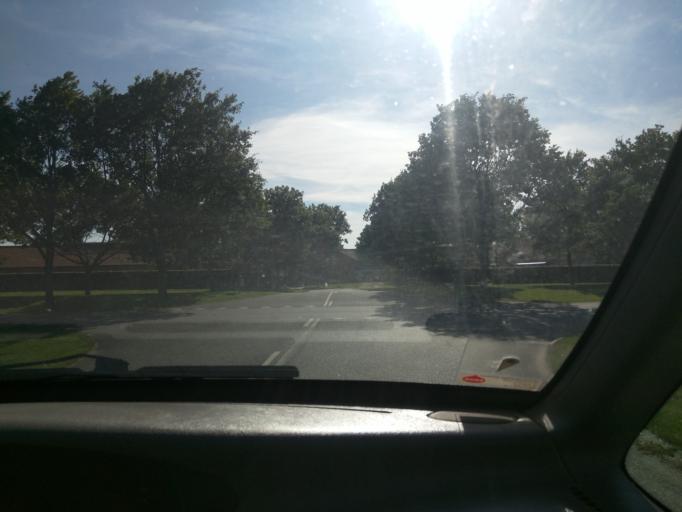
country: DK
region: Central Jutland
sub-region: Viborg Kommune
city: Bjerringbro
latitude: 56.4899
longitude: 9.5857
